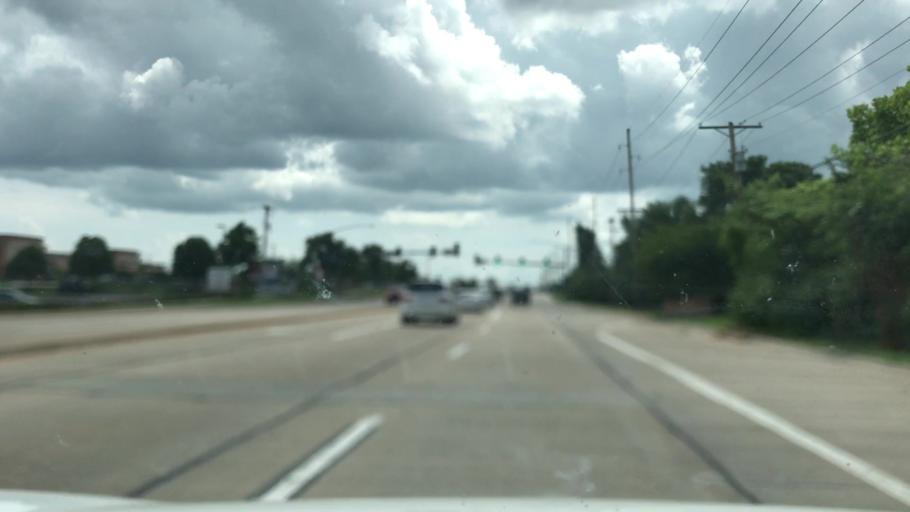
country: US
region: Missouri
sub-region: Saint Charles County
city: O'Fallon
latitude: 38.7847
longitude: -90.6999
